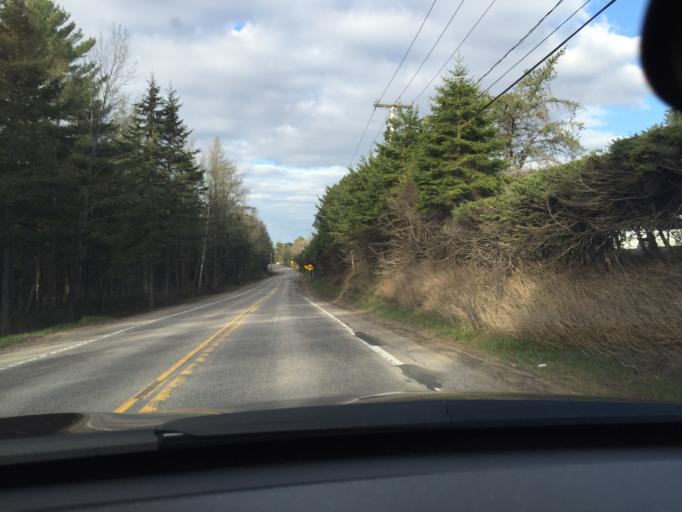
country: CA
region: Quebec
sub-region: Capitale-Nationale
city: Shannon
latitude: 46.8578
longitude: -71.5598
